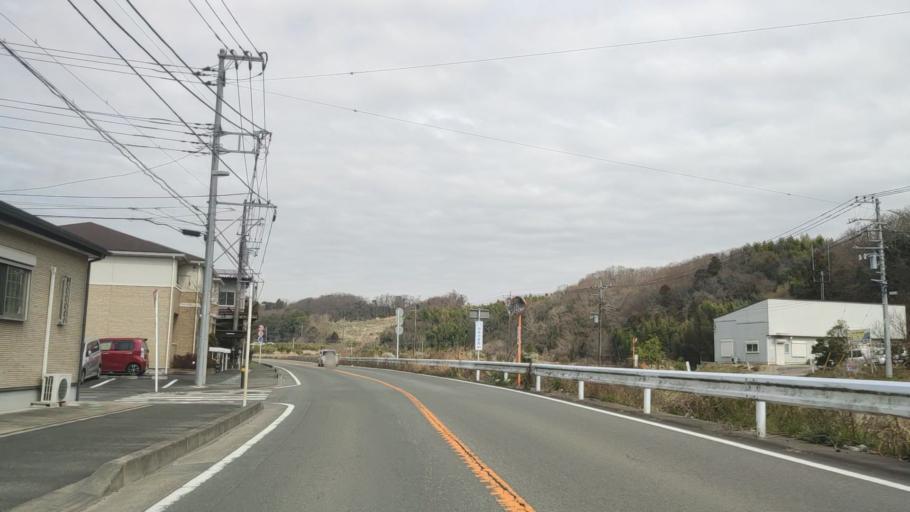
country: JP
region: Kanagawa
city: Ninomiya
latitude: 35.3241
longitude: 139.2185
